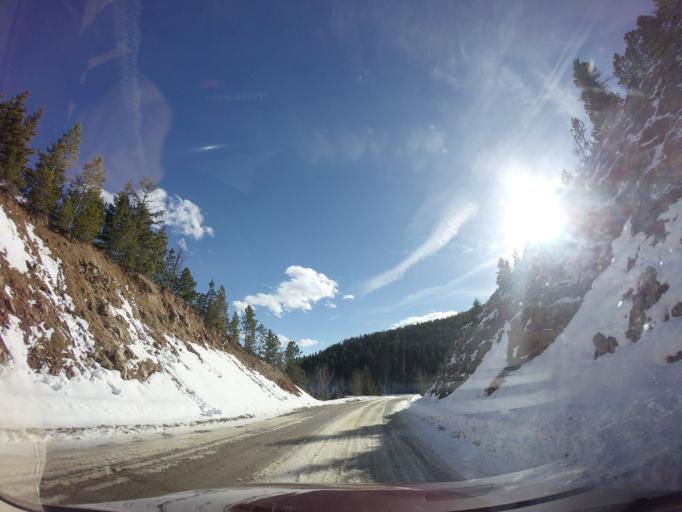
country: US
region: Montana
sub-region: Carbon County
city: Red Lodge
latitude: 45.1801
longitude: -109.3212
